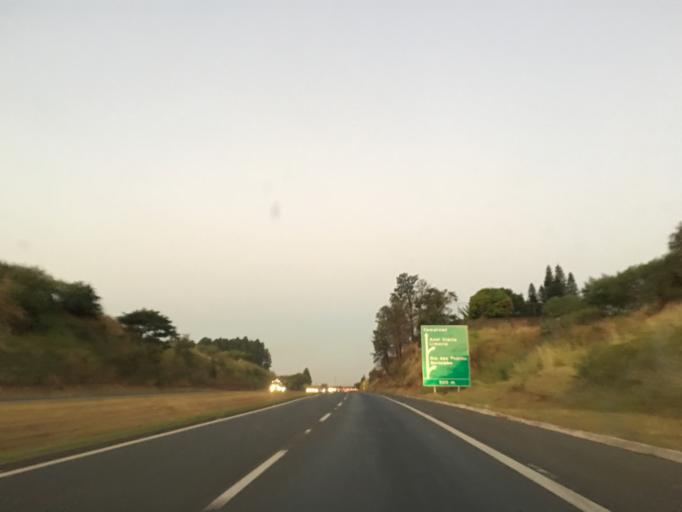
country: BR
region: Sao Paulo
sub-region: Piracicaba
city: Piracicaba
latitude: -22.7207
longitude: -47.6162
